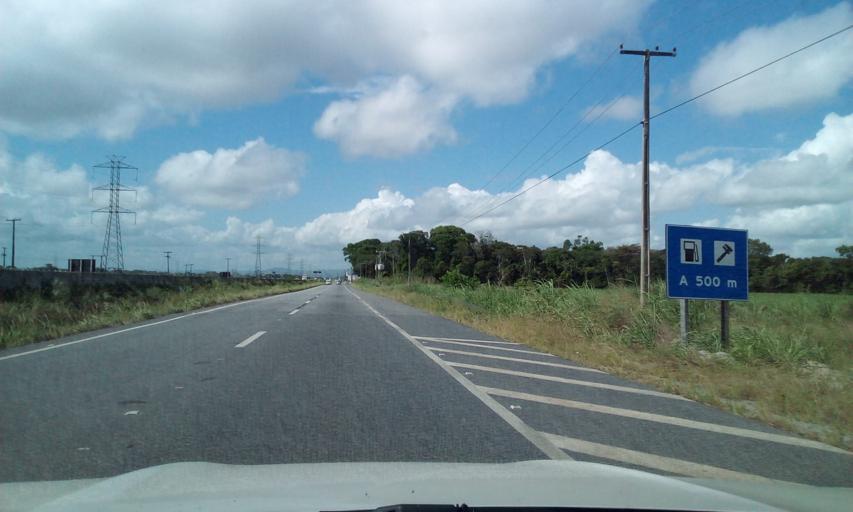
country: BR
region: Alagoas
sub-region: Rio Largo
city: Rio Largo
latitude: -9.4366
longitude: -35.8364
